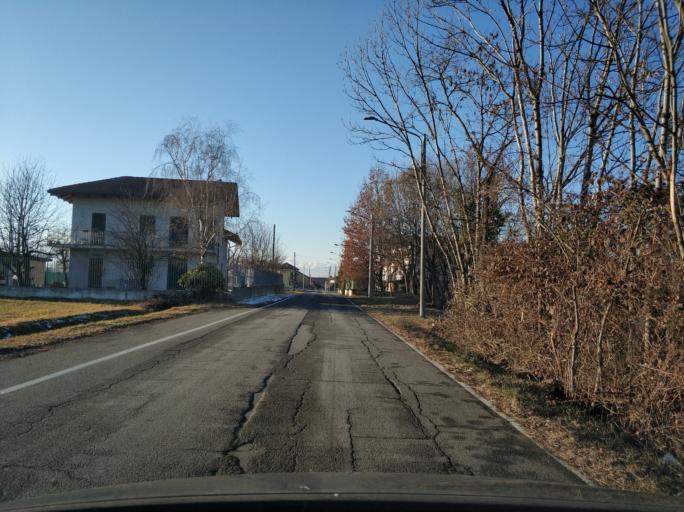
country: IT
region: Piedmont
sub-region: Provincia di Torino
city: San Francesco al Campo
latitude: 45.2282
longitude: 7.6528
